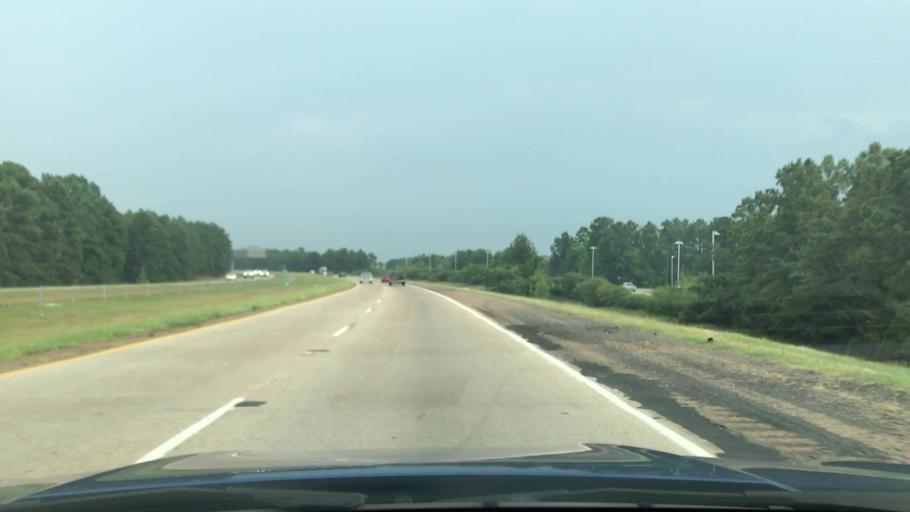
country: US
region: Louisiana
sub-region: Caddo Parish
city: Shreveport
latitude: 32.4274
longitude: -93.8389
